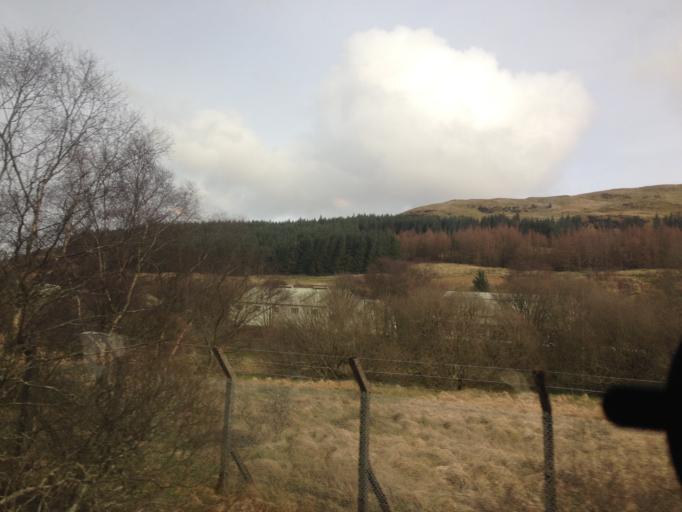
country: GB
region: Scotland
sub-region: Argyll and Bute
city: Garelochhead
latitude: 56.1509
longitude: -4.7823
